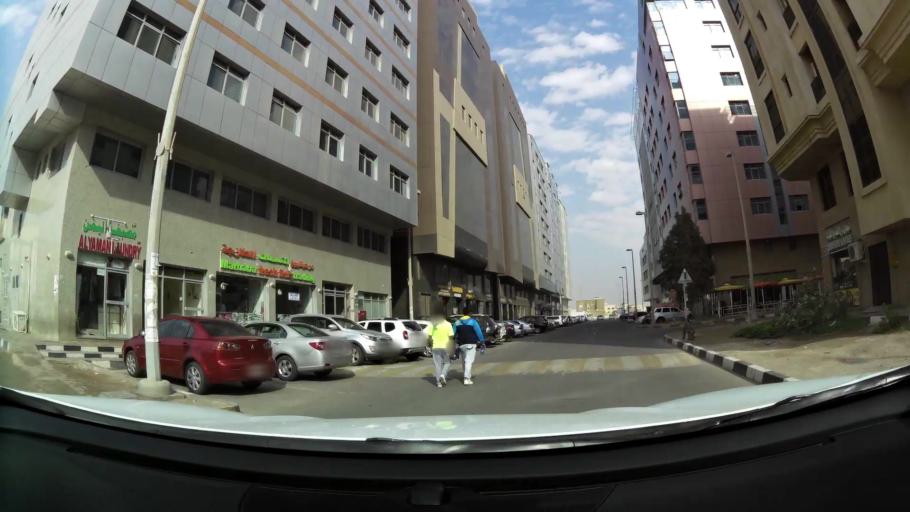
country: AE
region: Abu Dhabi
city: Abu Dhabi
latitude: 24.3201
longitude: 54.5375
